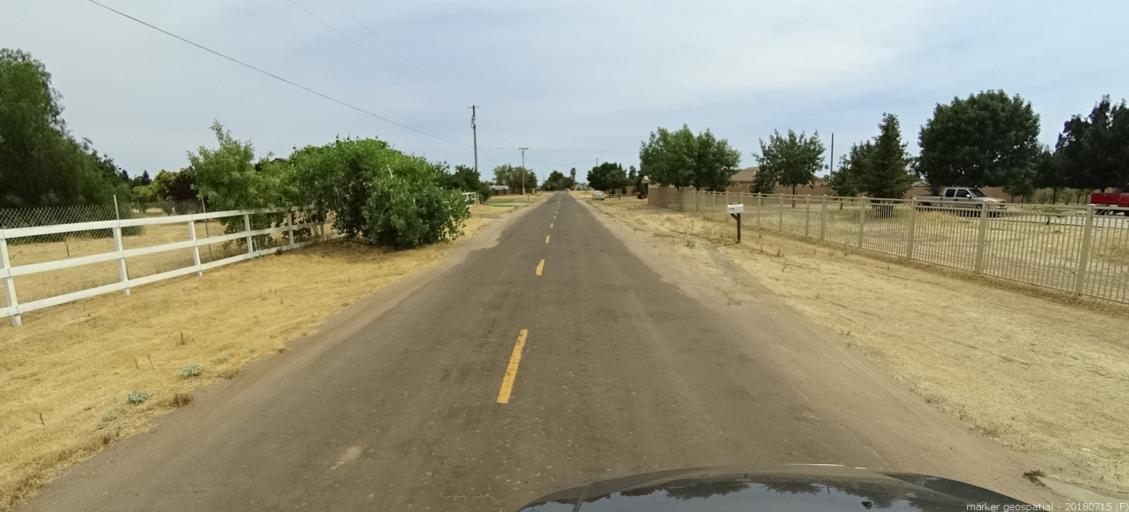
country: US
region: California
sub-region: Madera County
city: Madera Acres
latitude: 37.0069
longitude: -120.1018
